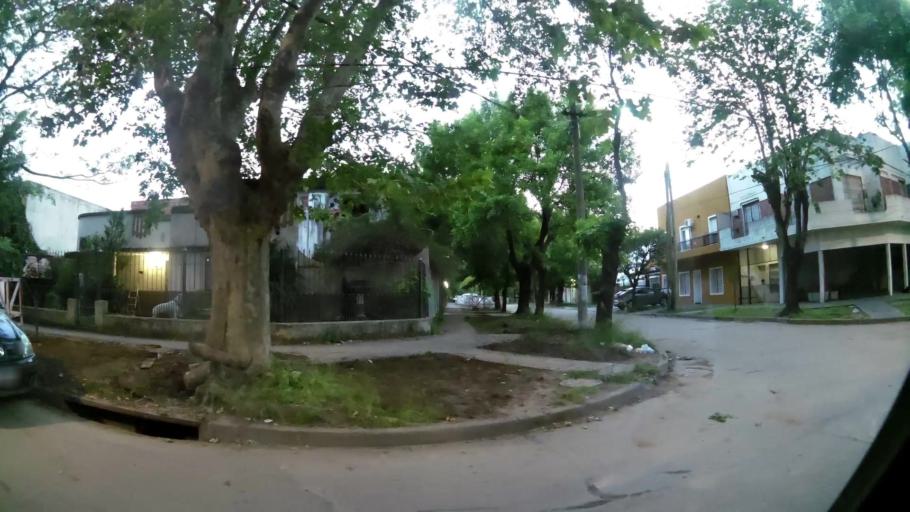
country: AR
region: Buenos Aires
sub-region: Partido de Quilmes
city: Quilmes
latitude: -34.8093
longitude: -58.2817
